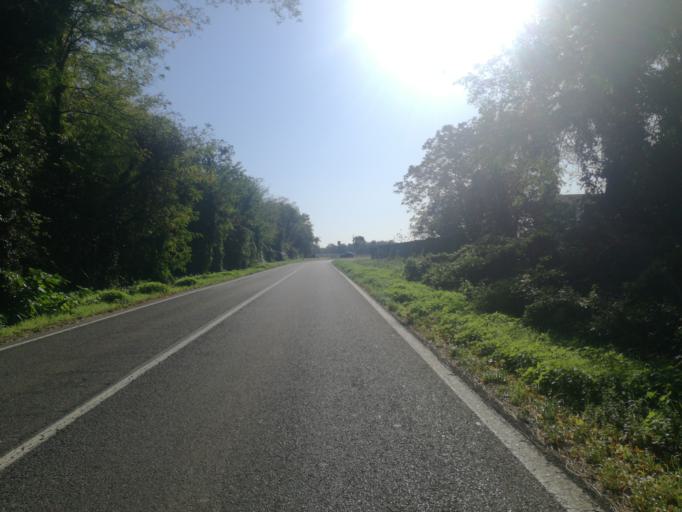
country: IT
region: Lombardy
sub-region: Provincia di Bergamo
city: Bottanuco
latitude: 45.6318
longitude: 9.4922
